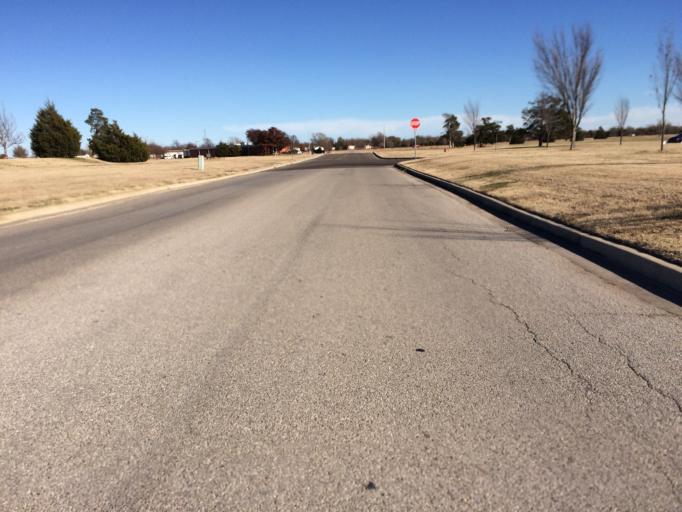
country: US
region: Oklahoma
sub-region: Cleveland County
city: Norman
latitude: 35.2379
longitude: -97.4597
